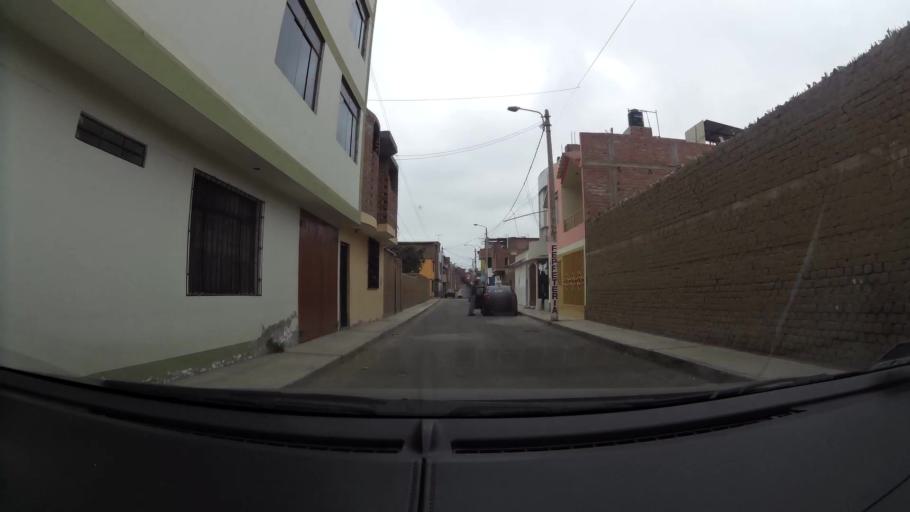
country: PE
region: La Libertad
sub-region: Provincia de Trujillo
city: Trujillo
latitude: -8.1040
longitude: -79.0430
